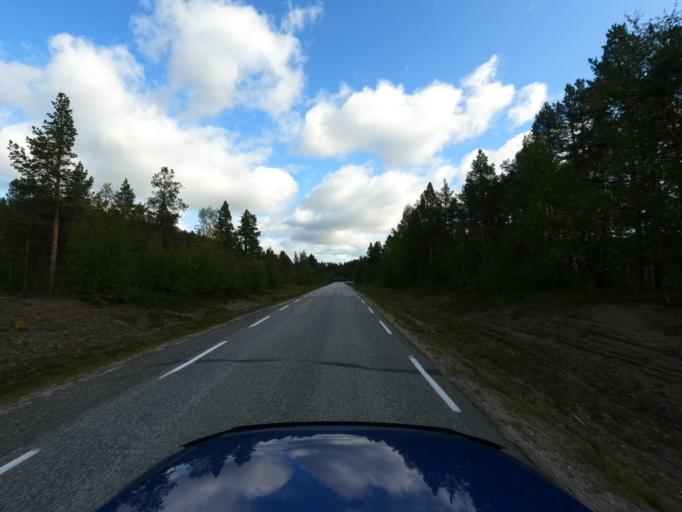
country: NO
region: Finnmark Fylke
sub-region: Karasjok
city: Karasjohka
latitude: 69.4358
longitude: 25.1589
